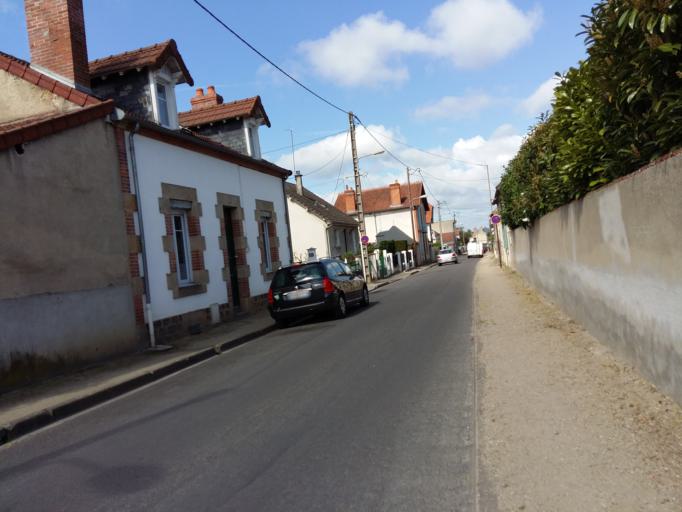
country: FR
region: Auvergne
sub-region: Departement de l'Allier
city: Moulins
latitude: 46.5723
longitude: 3.3391
